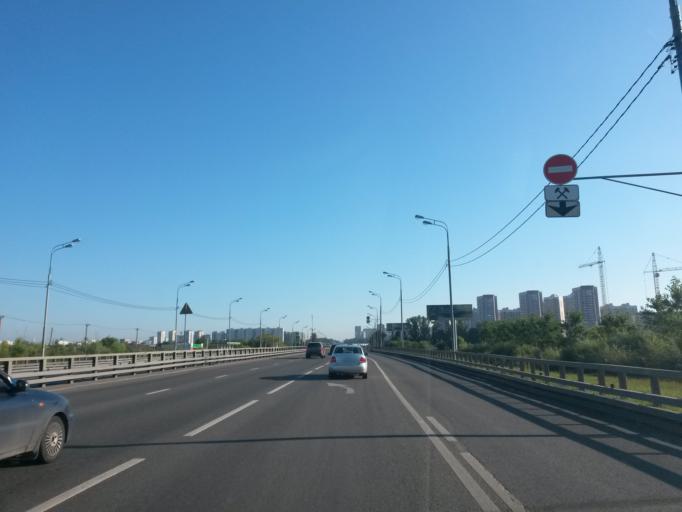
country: RU
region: Moskovskaya
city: Shcherbinka
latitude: 55.5225
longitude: 37.5783
